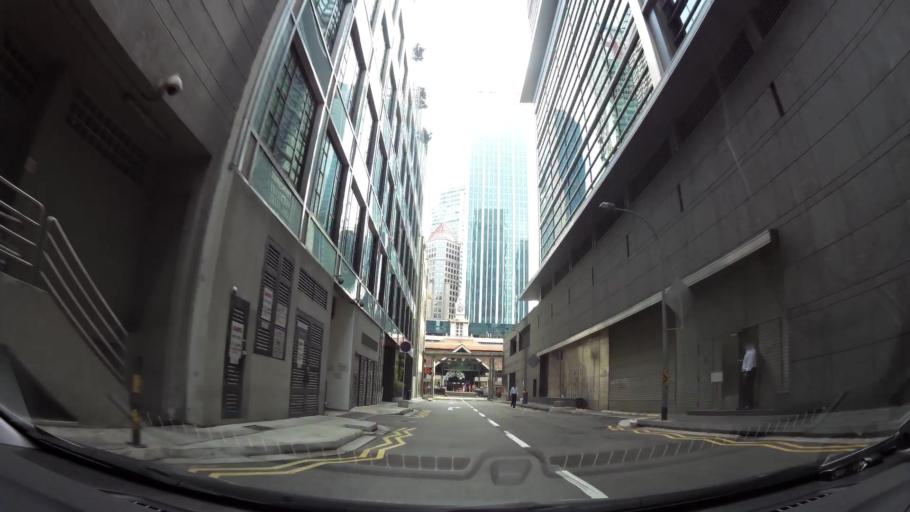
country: SG
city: Singapore
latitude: 1.2797
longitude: 103.8499
